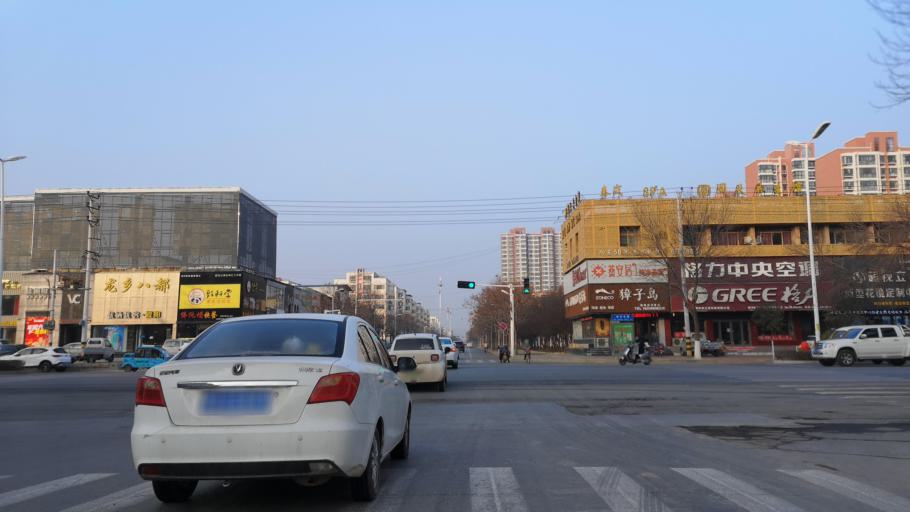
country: CN
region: Henan Sheng
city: Zhongyuanlu
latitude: 35.7695
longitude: 115.0638
